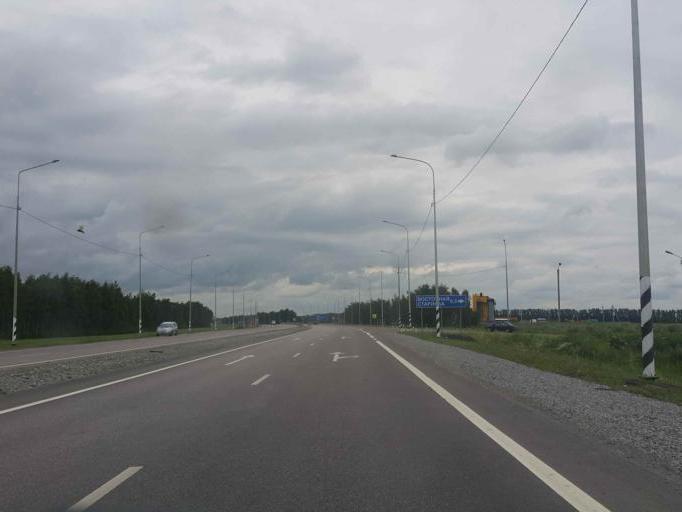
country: RU
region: Tambov
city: Zavoronezhskoye
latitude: 52.8618
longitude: 40.7662
